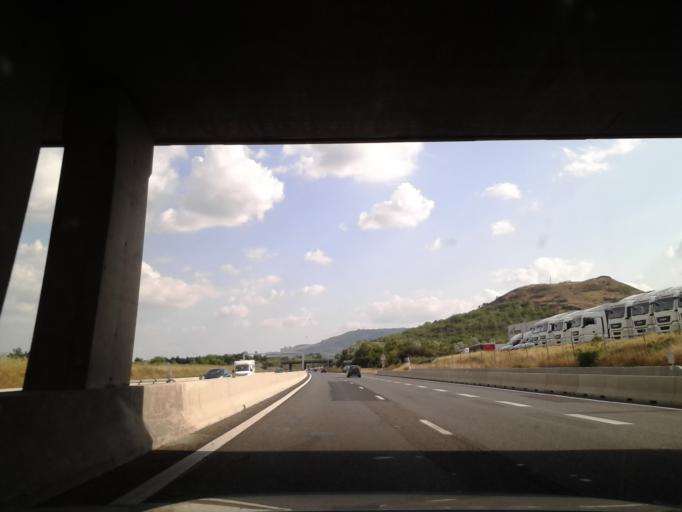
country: FR
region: Auvergne
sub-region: Departement du Puy-de-Dome
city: Aulnat
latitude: 45.7792
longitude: 3.1411
